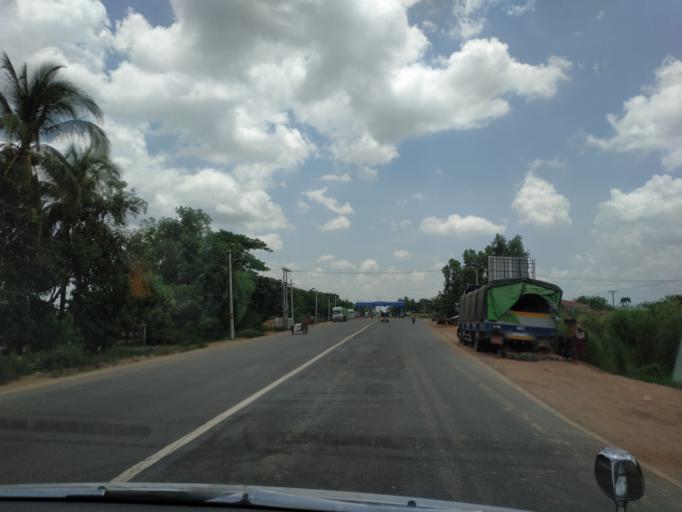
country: MM
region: Bago
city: Bago
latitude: 17.4718
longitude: 96.5444
